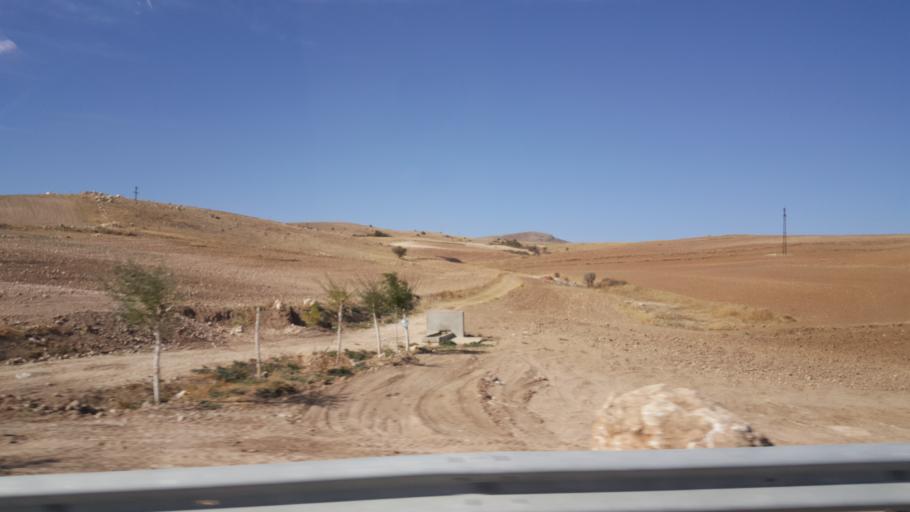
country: TR
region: Ankara
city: Ikizce
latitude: 39.5457
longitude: 32.6491
